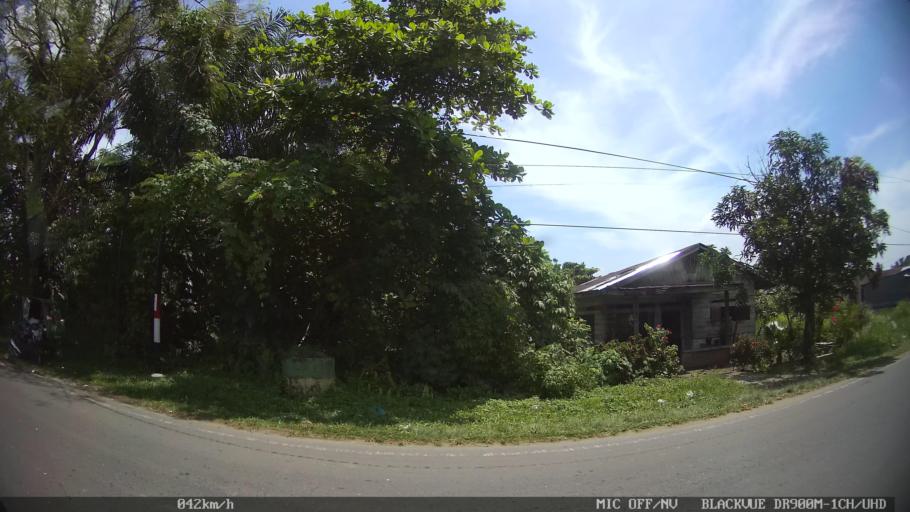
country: ID
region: North Sumatra
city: Binjai
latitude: 3.5970
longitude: 98.5001
